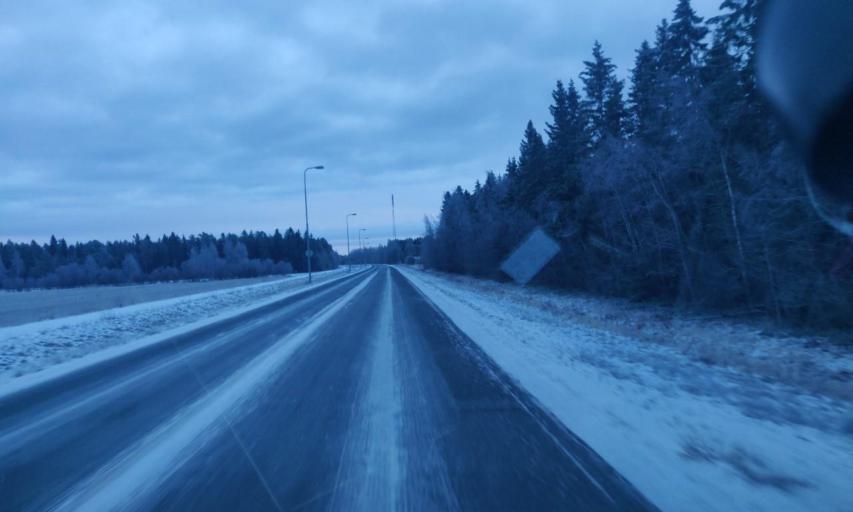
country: FI
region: Northern Ostrobothnia
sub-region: Oulu
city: Oulunsalo
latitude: 64.9783
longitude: 25.2785
